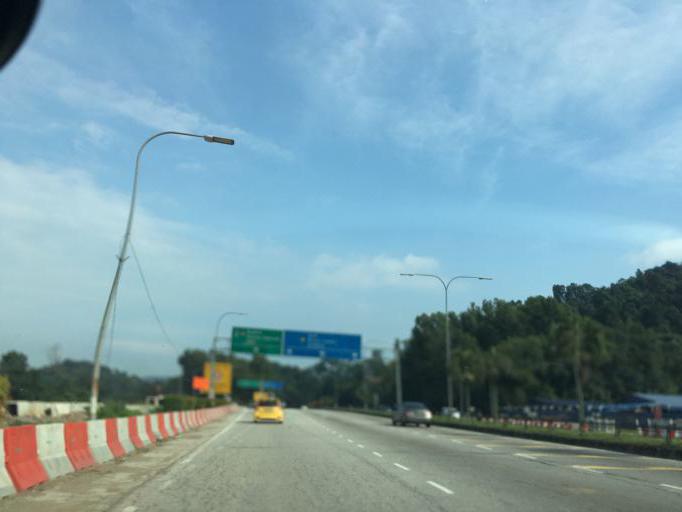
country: MY
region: Kuala Lumpur
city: Kuala Lumpur
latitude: 3.2361
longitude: 101.7233
